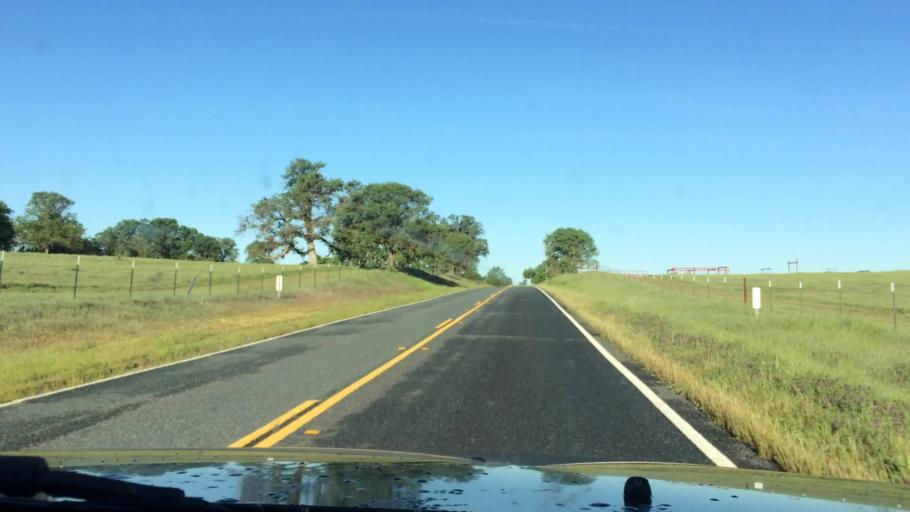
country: US
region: California
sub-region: Amador County
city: Ione
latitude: 38.3862
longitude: -121.0409
